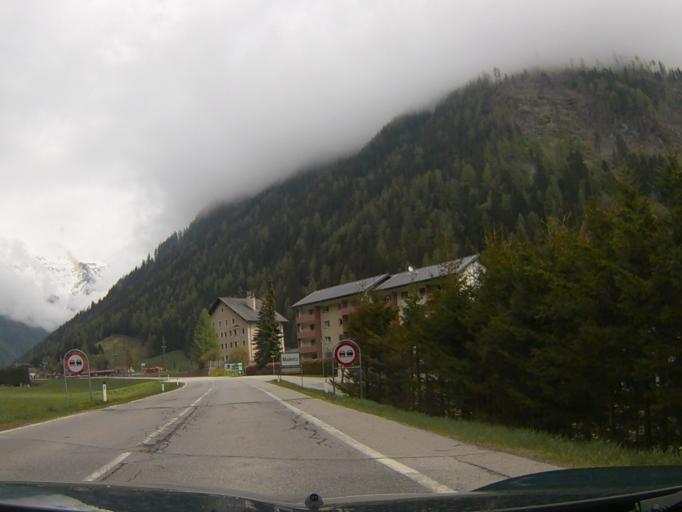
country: AT
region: Carinthia
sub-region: Politischer Bezirk Spittal an der Drau
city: Obervellach
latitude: 46.9769
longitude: 13.1768
